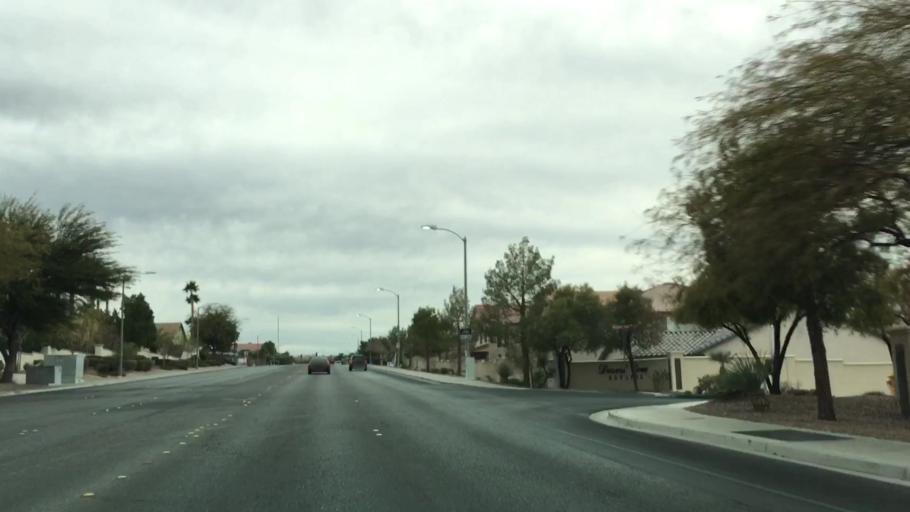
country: US
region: Nevada
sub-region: Clark County
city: Whitney
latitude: 36.0095
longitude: -115.0957
